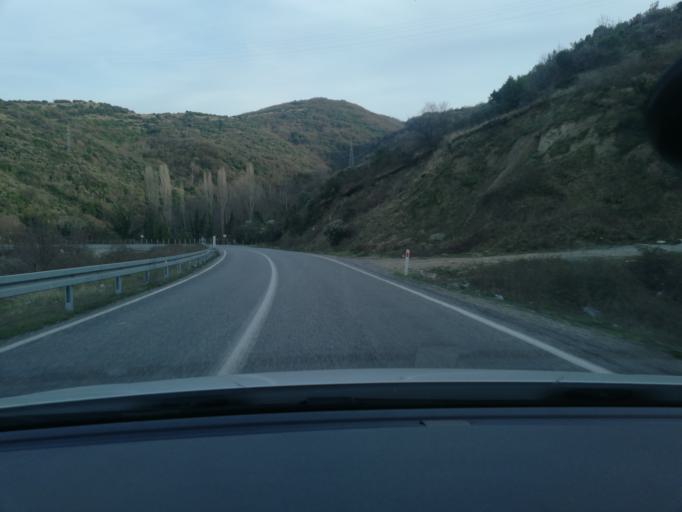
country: TR
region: Zonguldak
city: Tieum
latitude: 41.5468
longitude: 32.0009
